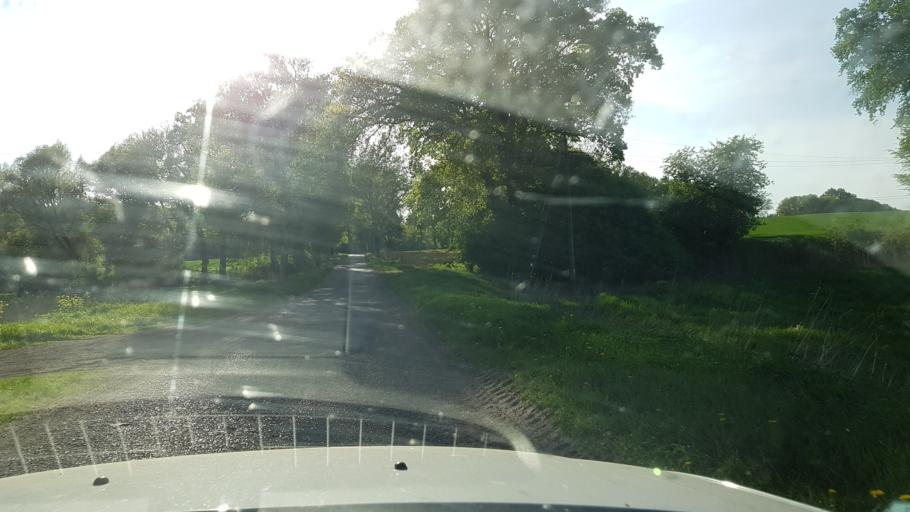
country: PL
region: West Pomeranian Voivodeship
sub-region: Powiat lobeski
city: Dobra
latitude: 53.6354
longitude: 15.3687
